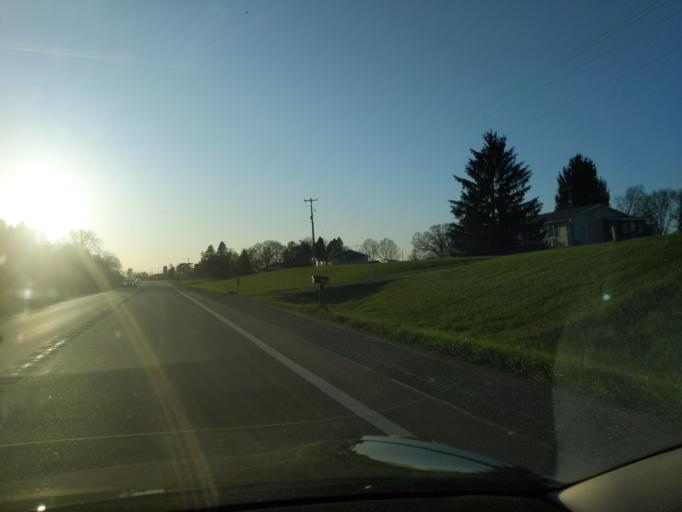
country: US
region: Michigan
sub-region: Ingham County
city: Stockbridge
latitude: 42.4146
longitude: -84.1396
